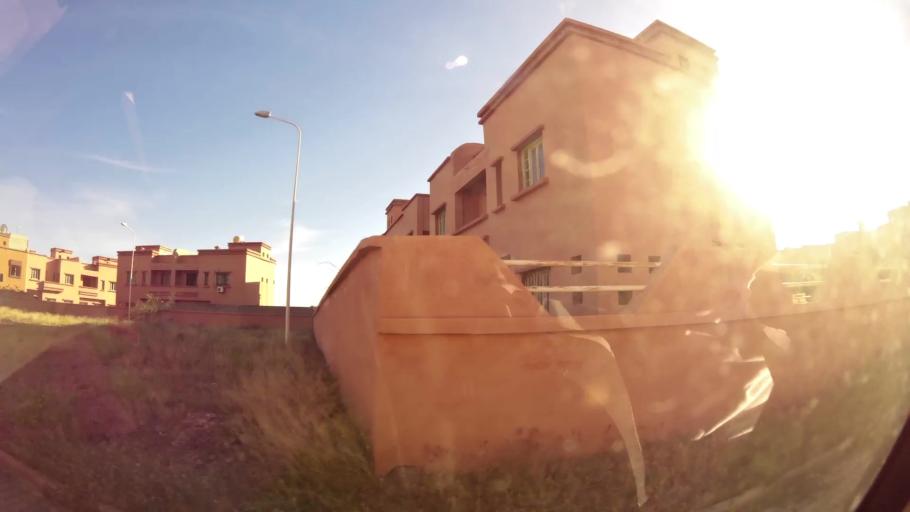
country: MA
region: Marrakech-Tensift-Al Haouz
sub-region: Marrakech
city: Marrakesh
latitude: 31.7581
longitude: -8.1058
